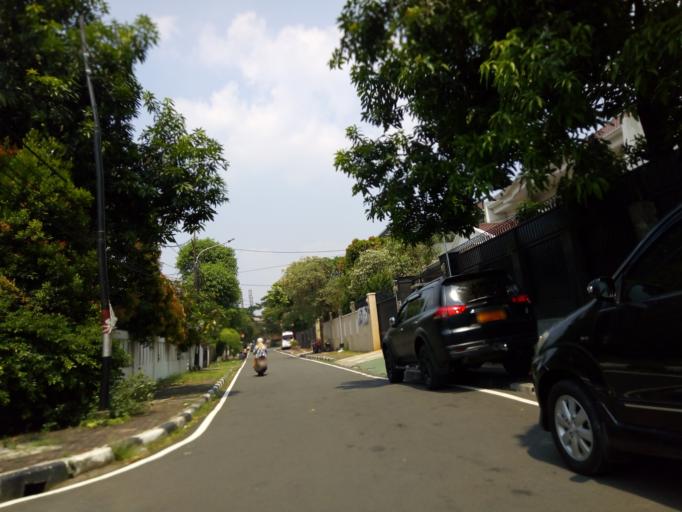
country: ID
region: Jakarta Raya
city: Jakarta
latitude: -6.2039
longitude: 106.8365
